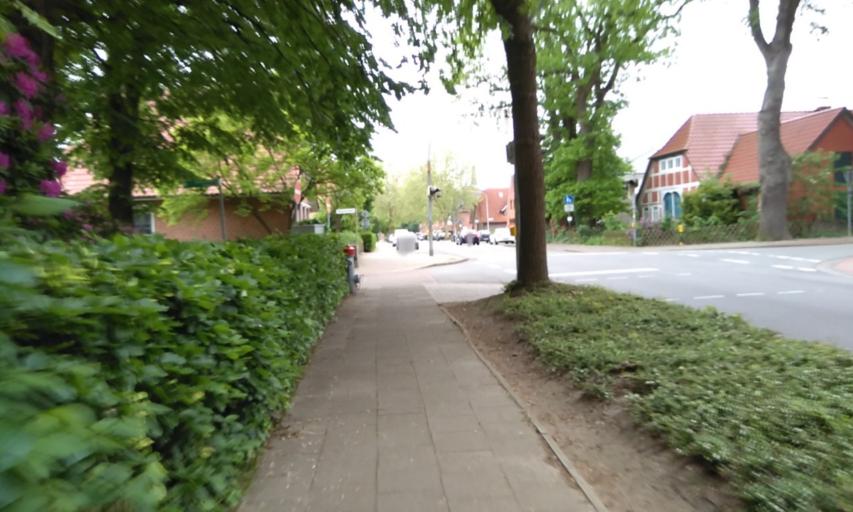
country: DE
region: Lower Saxony
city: Harsefeld
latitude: 53.4528
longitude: 9.4957
